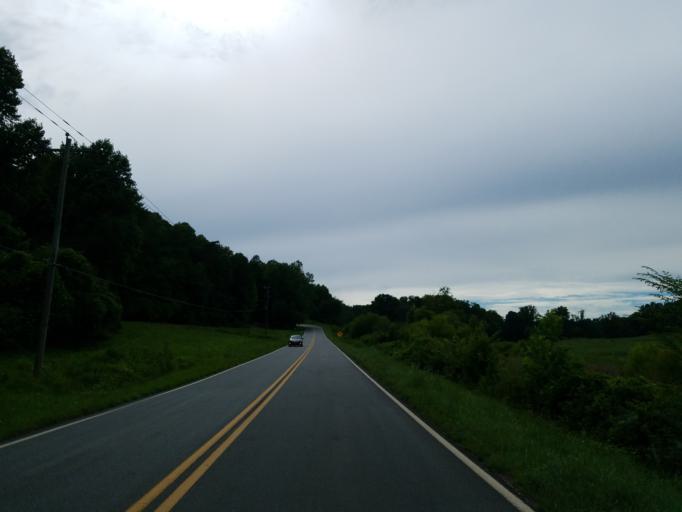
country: US
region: Georgia
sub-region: Lumpkin County
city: Dahlonega
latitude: 34.5656
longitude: -83.9585
